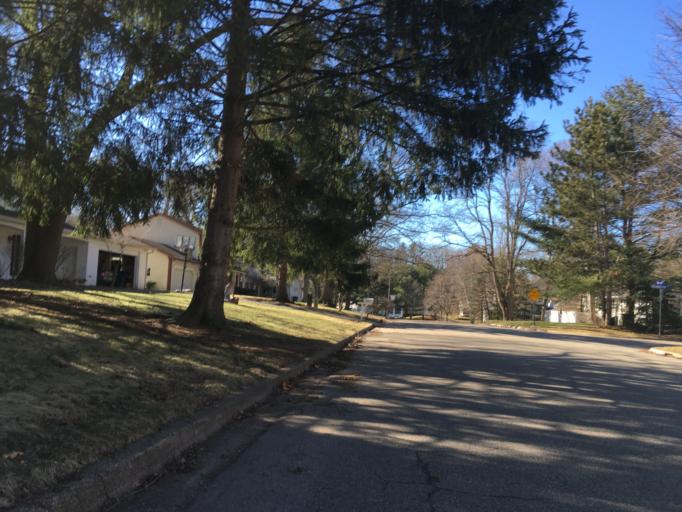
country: US
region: Michigan
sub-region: Kalamazoo County
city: Westwood
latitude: 42.2638
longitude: -85.6258
